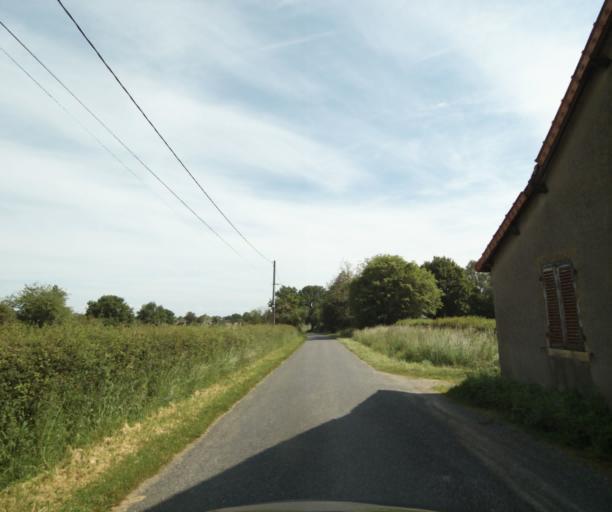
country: FR
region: Bourgogne
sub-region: Departement de Saone-et-Loire
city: Palinges
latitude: 46.5518
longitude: 4.1782
